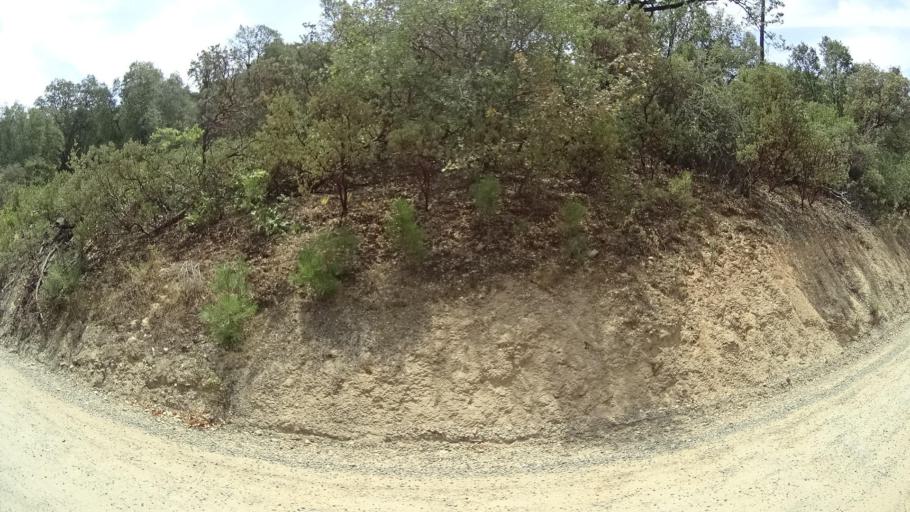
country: US
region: California
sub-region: Madera County
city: Ahwahnee
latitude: 37.4477
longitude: -119.8114
